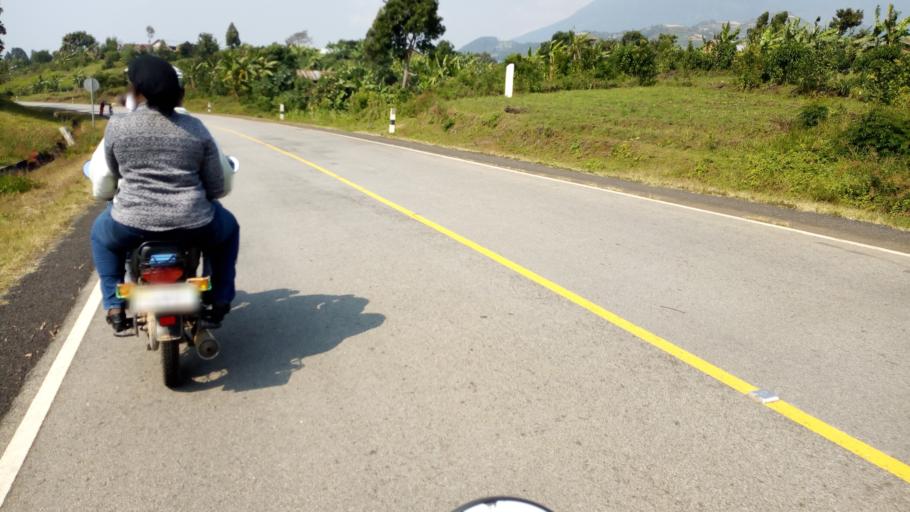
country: UG
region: Western Region
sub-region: Kisoro District
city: Kisoro
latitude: -1.3279
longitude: 29.7287
